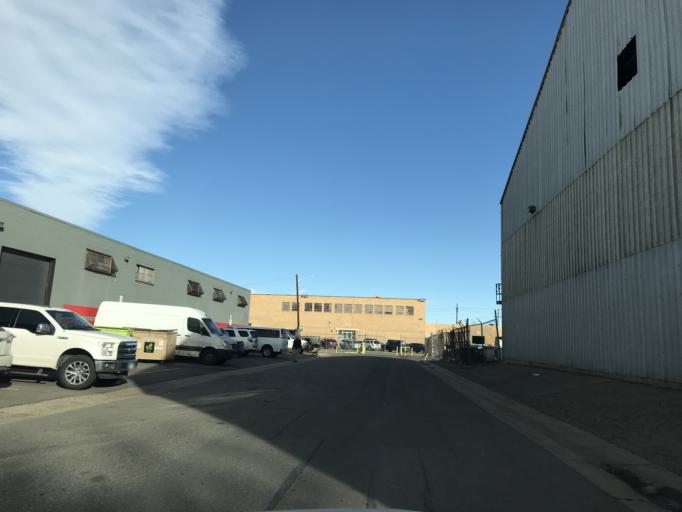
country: US
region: Colorado
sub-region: Denver County
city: Denver
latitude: 39.7693
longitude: -104.9635
